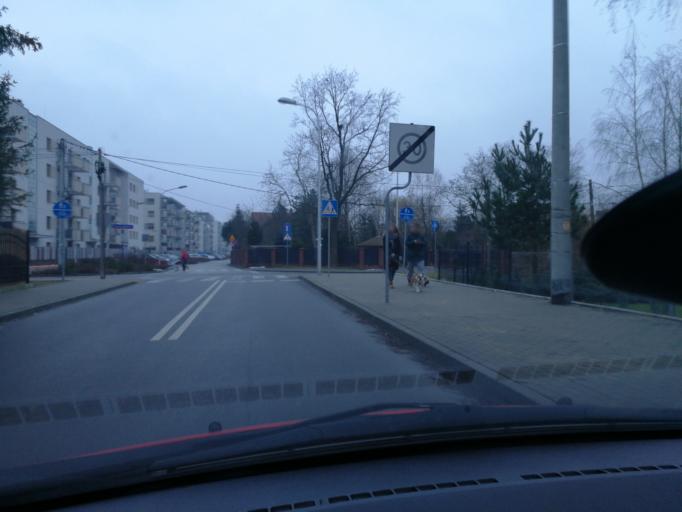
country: PL
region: Masovian Voivodeship
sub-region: Warszawa
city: Bemowo
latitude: 52.2321
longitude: 20.8916
